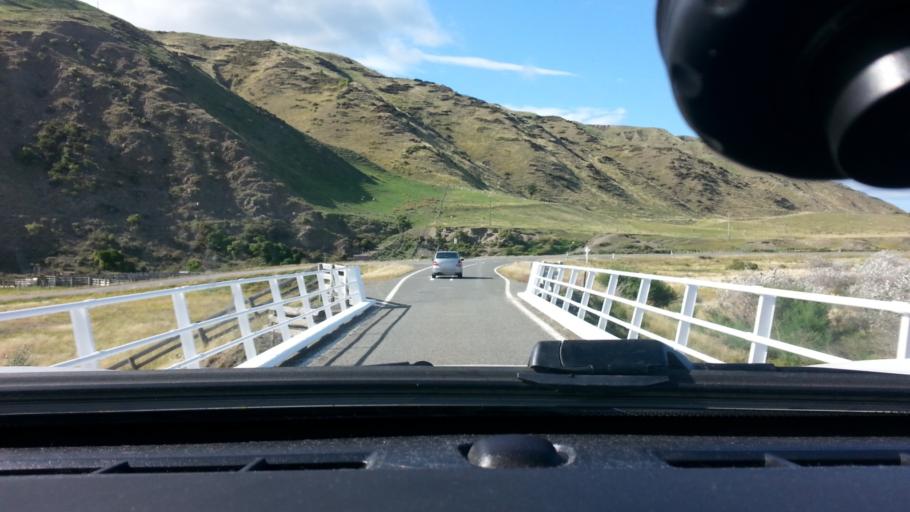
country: NZ
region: Wellington
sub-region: South Wairarapa District
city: Waipawa
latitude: -41.5498
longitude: 175.2248
